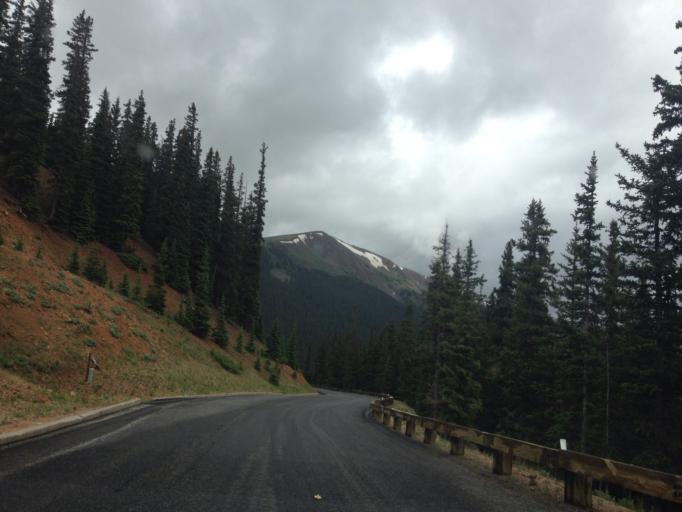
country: US
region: Colorado
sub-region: Clear Creek County
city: Georgetown
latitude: 39.6033
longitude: -105.7113
